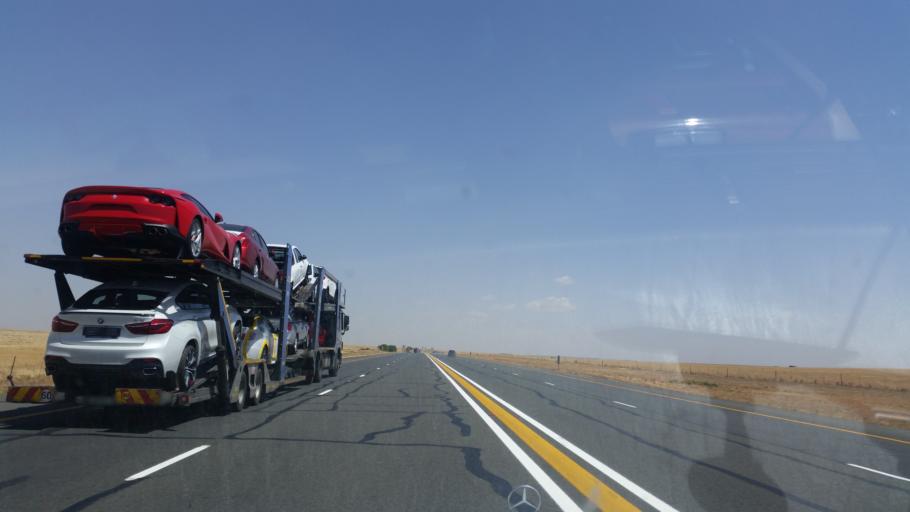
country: ZA
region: Orange Free State
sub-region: Lejweleputswa District Municipality
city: Brandfort
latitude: -28.8750
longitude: 26.5119
